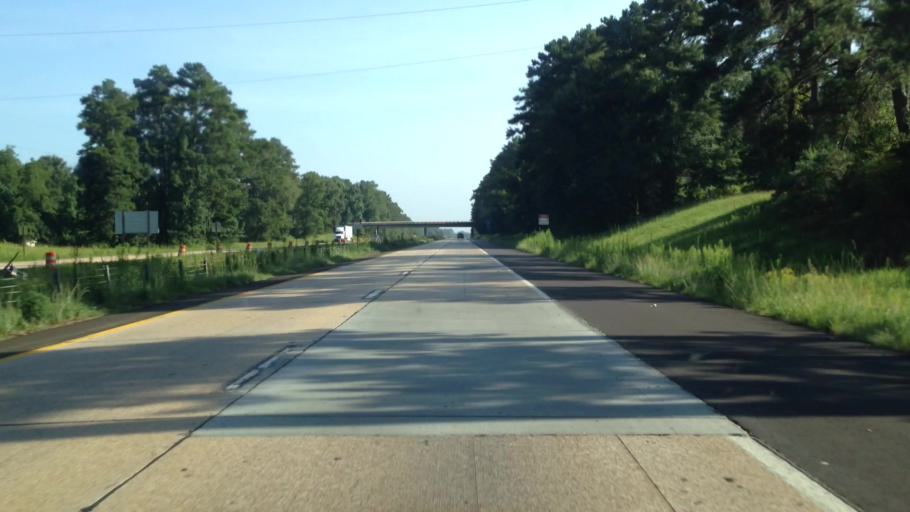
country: US
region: Mississippi
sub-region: Pike County
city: Summit
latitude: 31.2701
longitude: -90.4789
